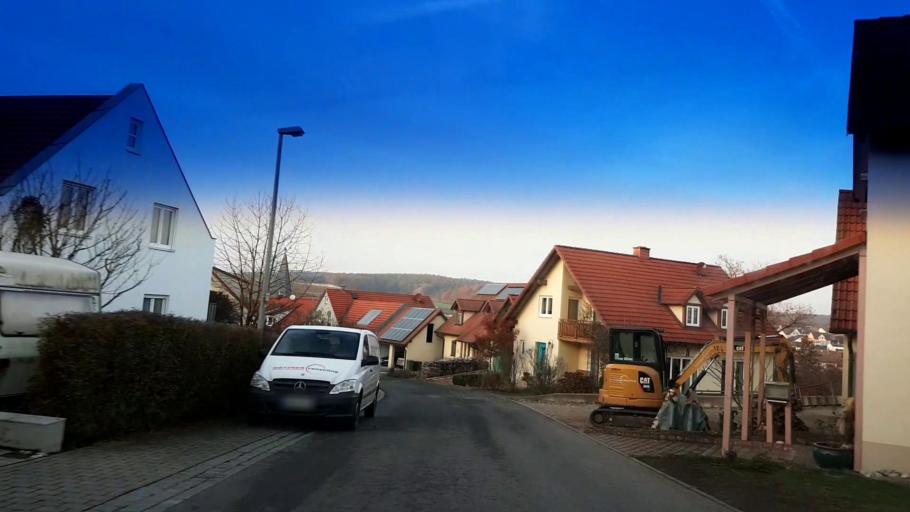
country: DE
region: Bavaria
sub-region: Upper Franconia
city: Walsdorf
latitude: 49.8668
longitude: 10.8131
